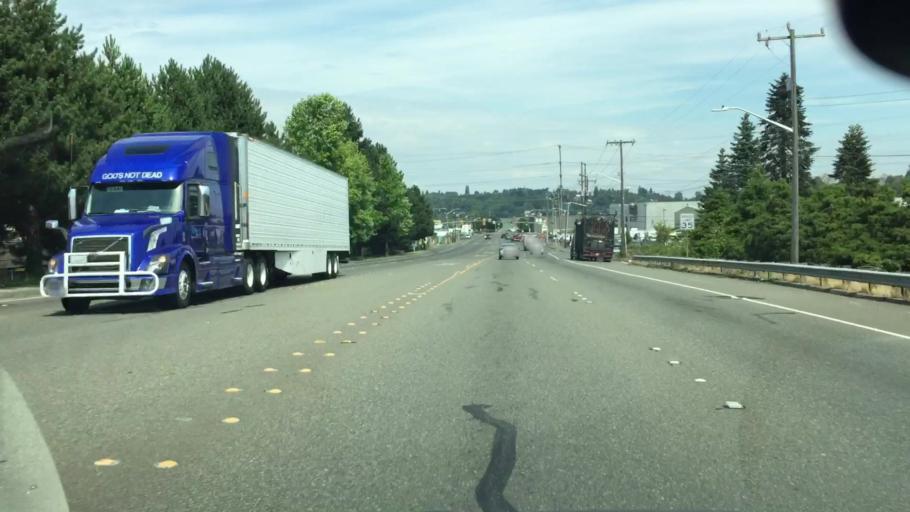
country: US
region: Washington
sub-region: King County
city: Riverton
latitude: 47.5010
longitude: -122.2942
